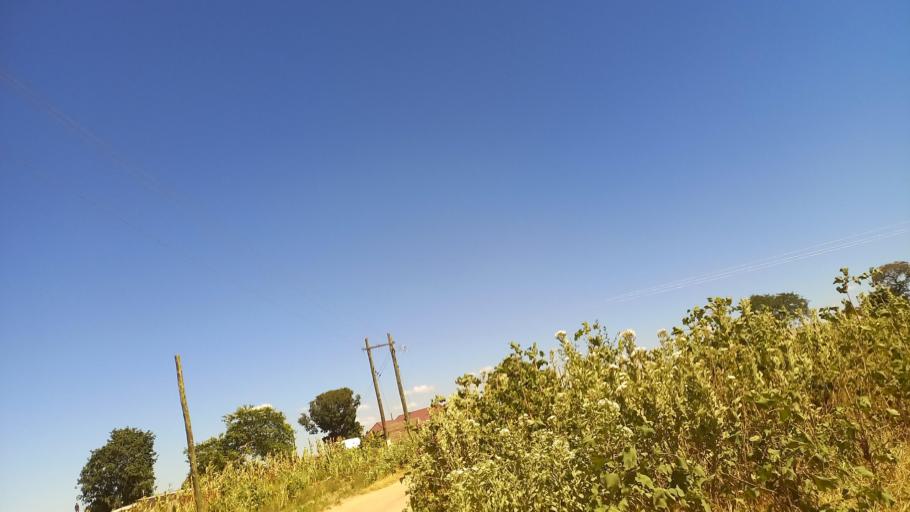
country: TZ
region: Dodoma
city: Dodoma
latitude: -6.1117
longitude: 35.7019
